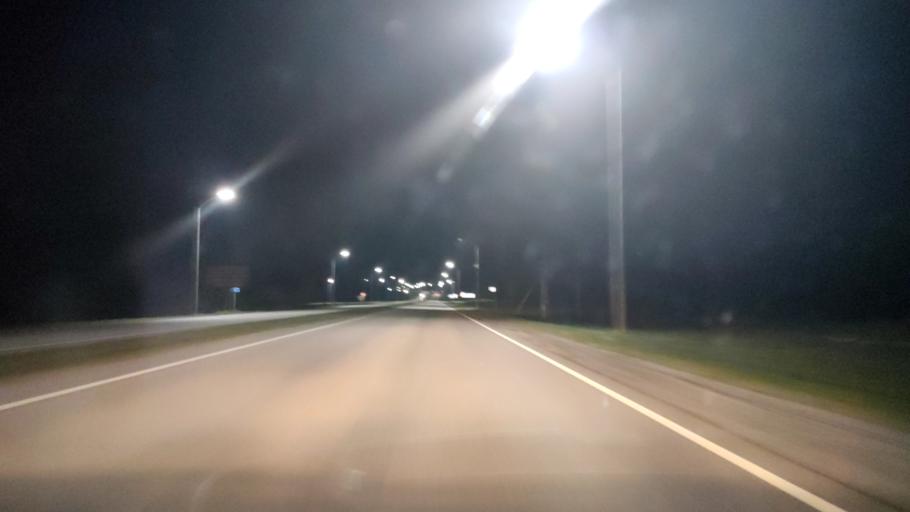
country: RU
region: Belgorod
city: Staryy Oskol
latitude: 51.3874
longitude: 37.8624
